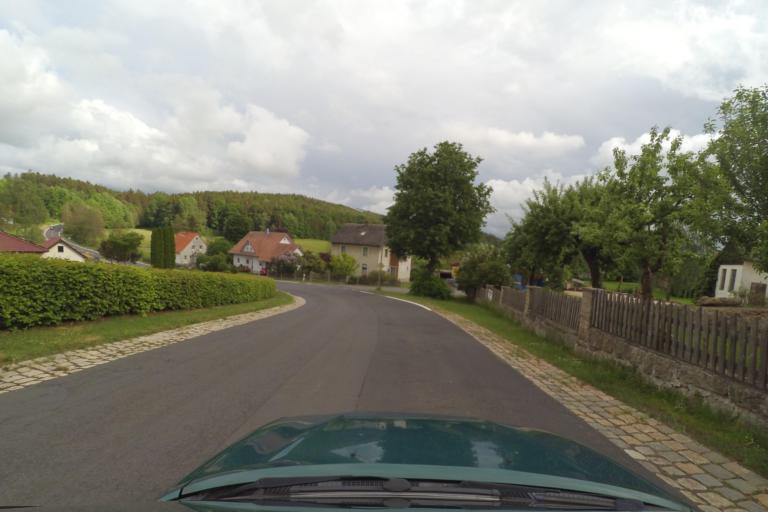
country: DE
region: Bavaria
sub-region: Upper Palatinate
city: Schwarzenbach
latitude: 49.8380
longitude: 12.3810
